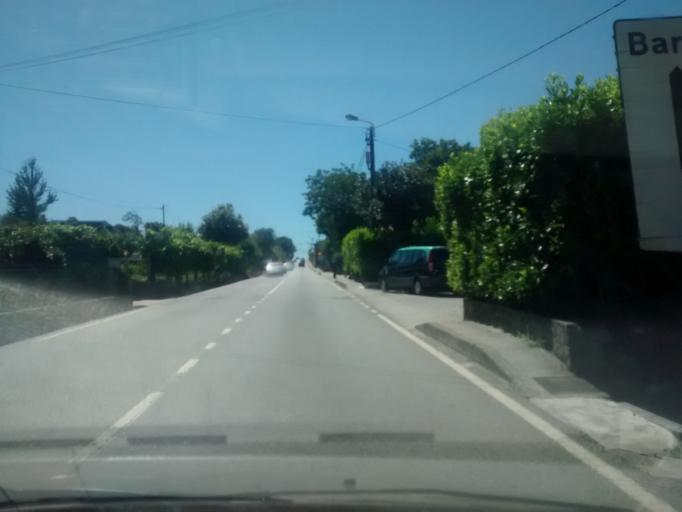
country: PT
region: Braga
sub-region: Barcelos
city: Galegos
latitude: 41.5334
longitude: -8.5116
